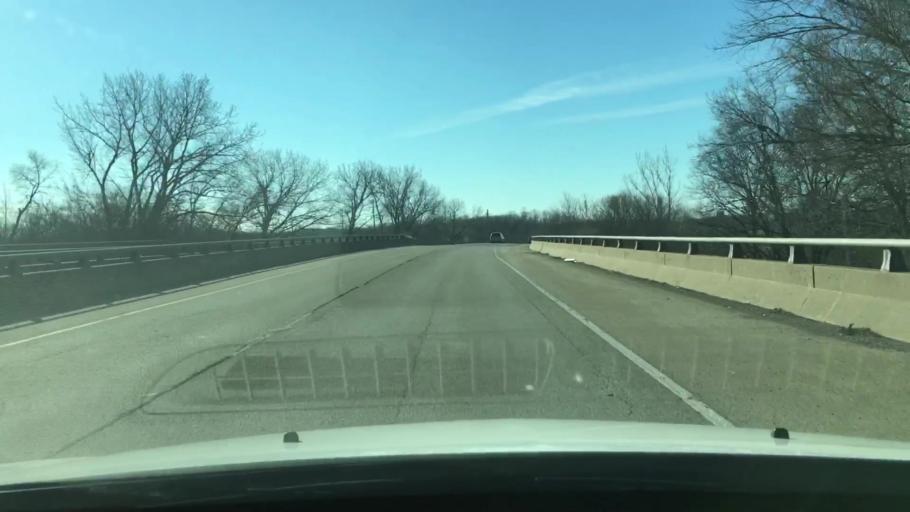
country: US
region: Illinois
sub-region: Tazewell County
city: Pekin
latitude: 40.5705
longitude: -89.7166
